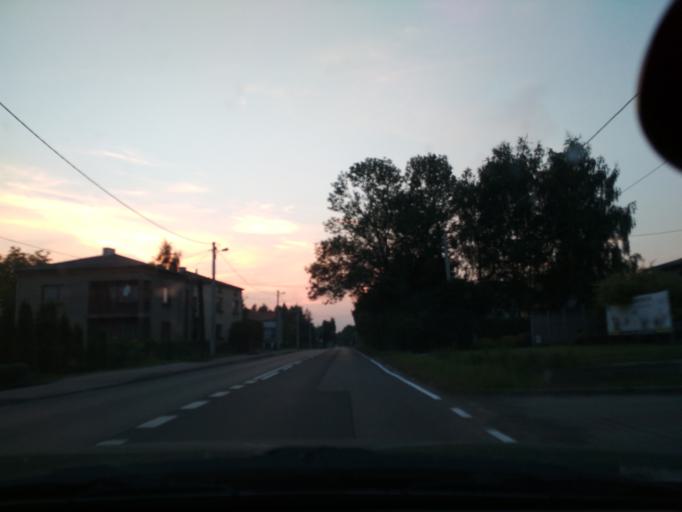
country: PL
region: Silesian Voivodeship
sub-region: Powiat zawiercianski
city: Ogrodzieniec
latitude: 50.4571
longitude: 19.5014
